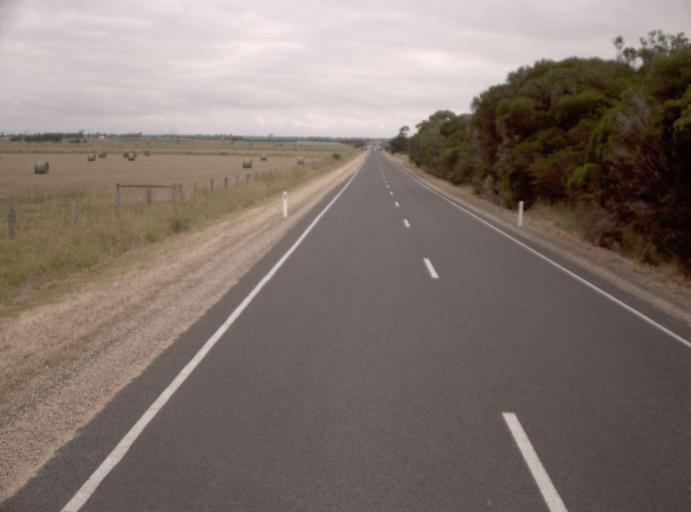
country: AU
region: Victoria
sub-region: Wellington
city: Sale
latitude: -38.0907
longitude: 146.9867
